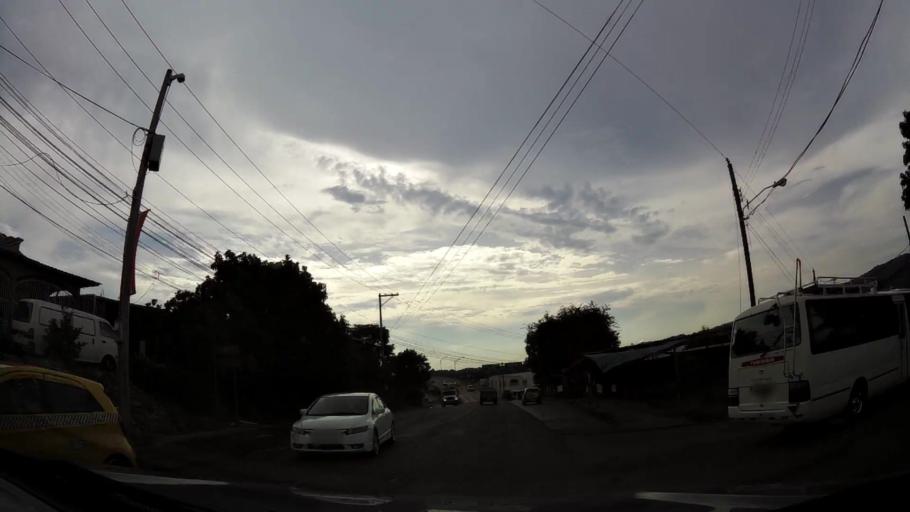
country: PA
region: Panama
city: Tocumen
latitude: 9.1039
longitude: -79.3640
